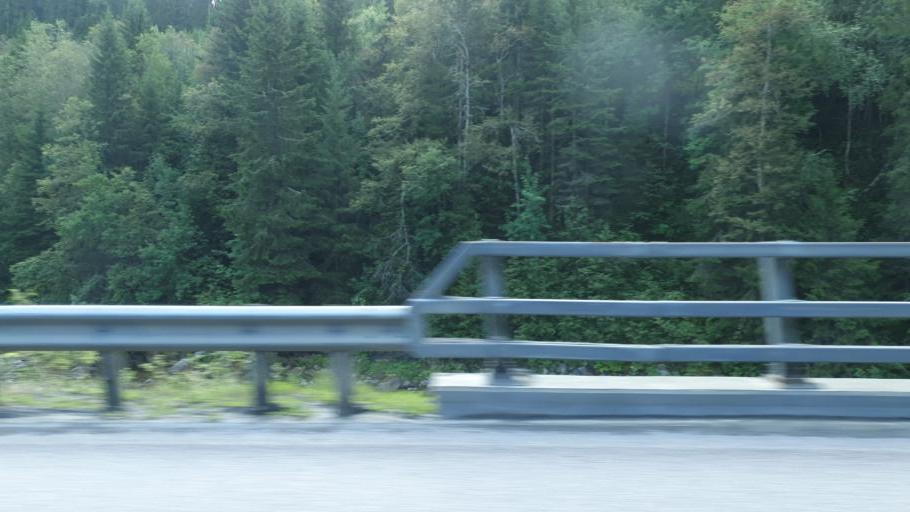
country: NO
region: Sor-Trondelag
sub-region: Midtre Gauldal
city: Storen
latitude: 62.9839
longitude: 10.2398
